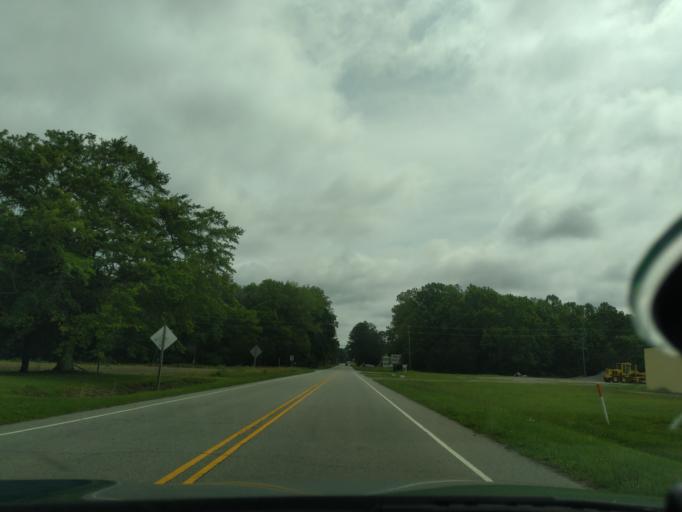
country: US
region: North Carolina
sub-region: Washington County
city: Plymouth
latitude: 35.8753
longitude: -76.6209
